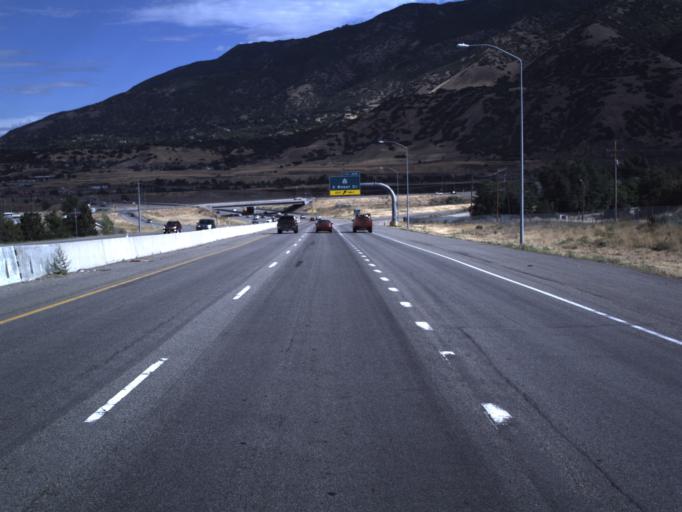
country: US
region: Utah
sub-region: Davis County
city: South Weber
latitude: 41.1228
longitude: -111.9081
